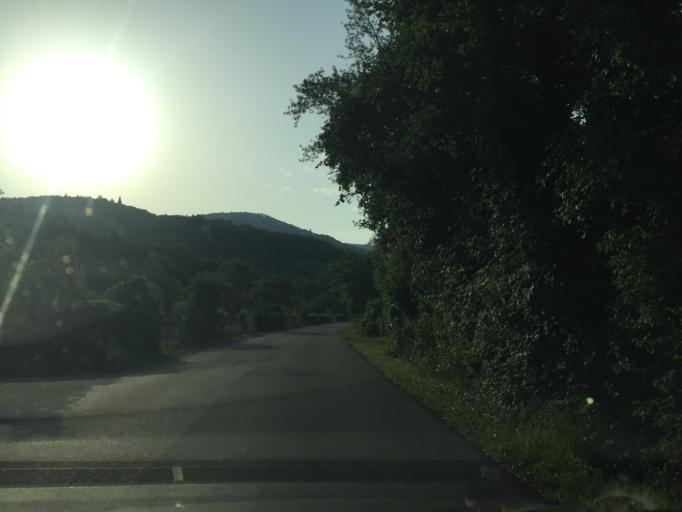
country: IT
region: Friuli Venezia Giulia
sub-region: Provincia di Trieste
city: Domio
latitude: 45.5884
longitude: 13.8300
